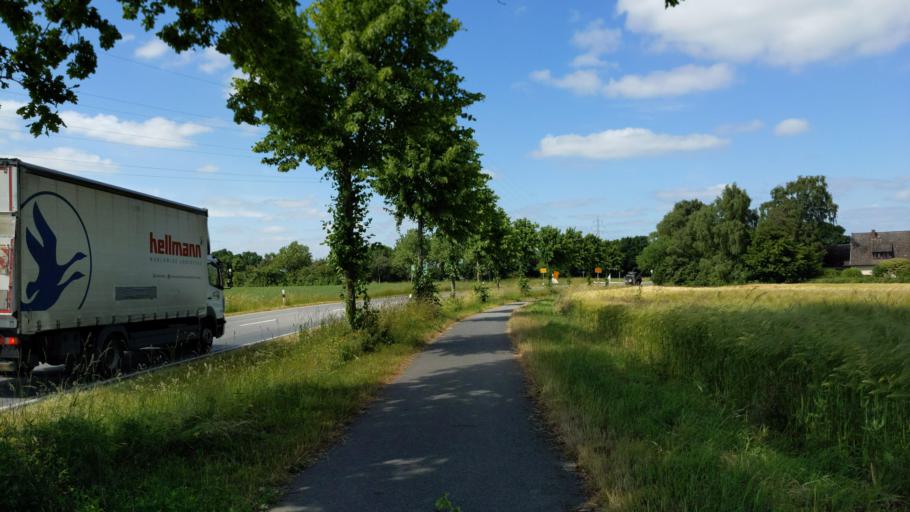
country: DE
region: Schleswig-Holstein
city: Scharbeutz
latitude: 54.0160
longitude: 10.7395
